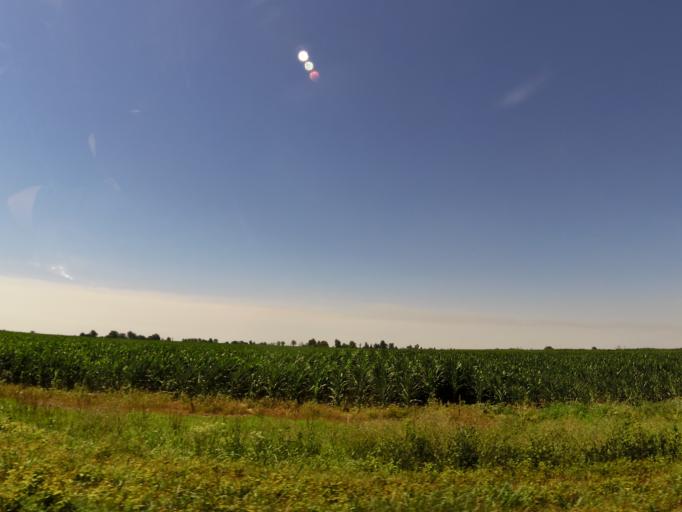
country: US
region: Missouri
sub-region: Dunklin County
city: Malden
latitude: 36.5534
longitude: -89.8468
